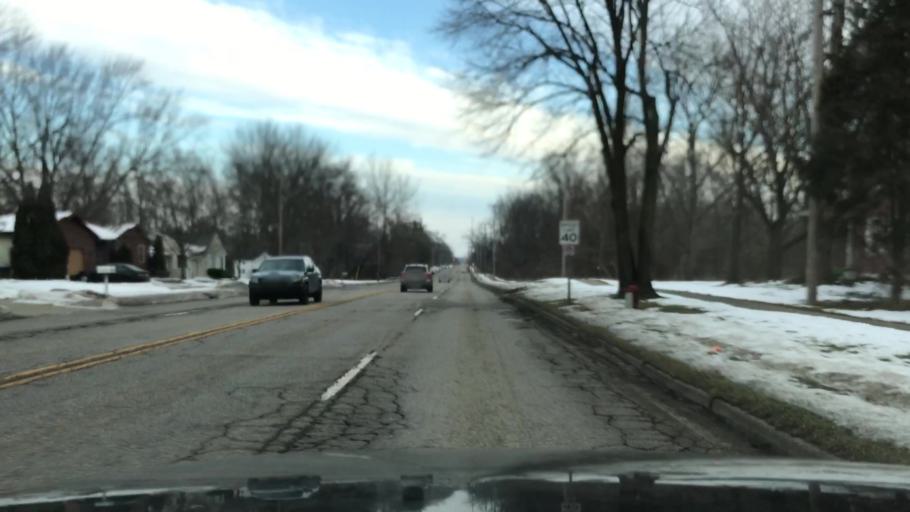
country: US
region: Michigan
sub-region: Kent County
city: Grandville
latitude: 42.8996
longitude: -85.7438
